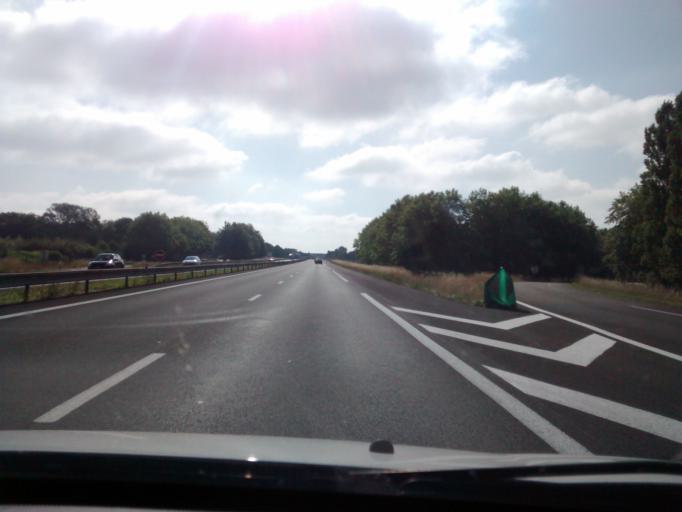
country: FR
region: Pays de la Loire
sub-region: Departement de la Mayenne
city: Vaiges
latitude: 48.0592
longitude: -0.5063
